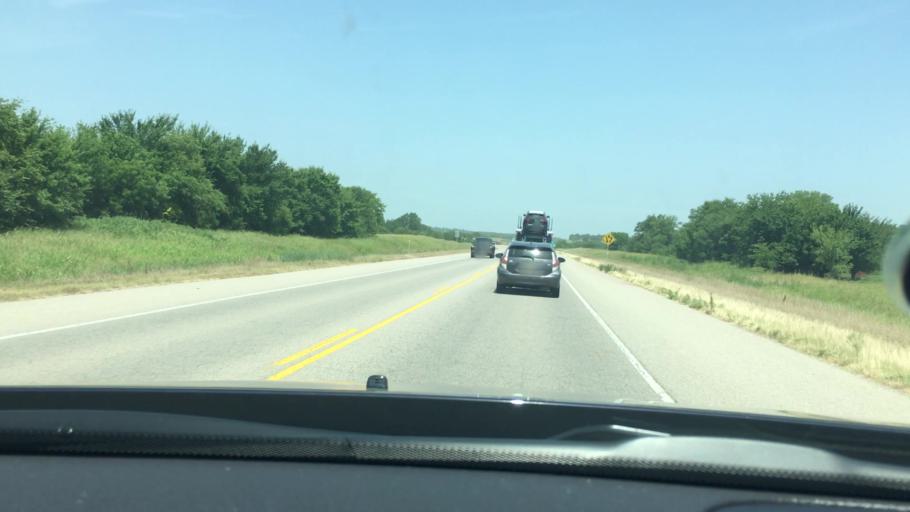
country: US
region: Oklahoma
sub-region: Pontotoc County
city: Ada
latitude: 34.7167
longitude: -96.6239
